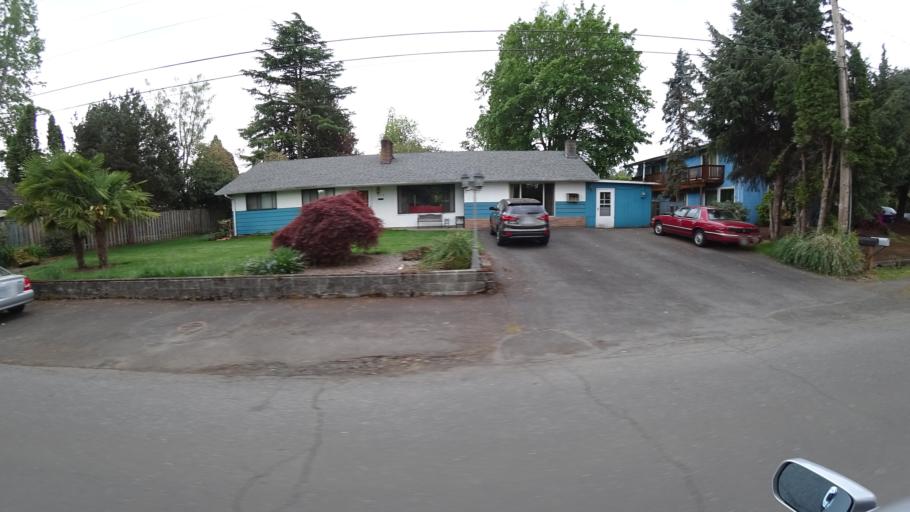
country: US
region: Oregon
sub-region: Washington County
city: Hillsboro
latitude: 45.5307
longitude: -122.9802
